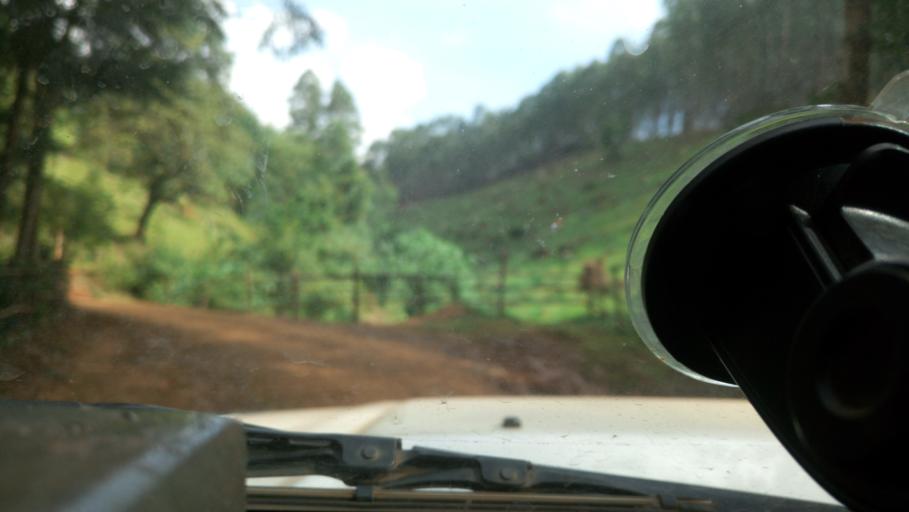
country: KE
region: Kericho
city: Sotik
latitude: -0.5767
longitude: 35.0718
